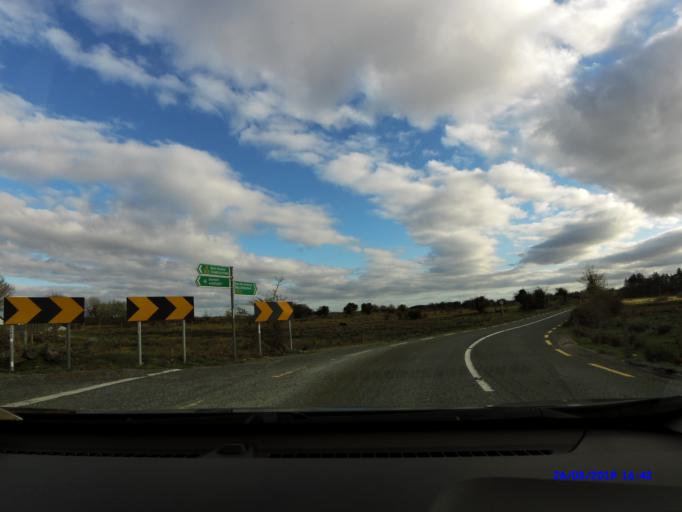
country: IE
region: Connaught
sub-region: Maigh Eo
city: Ballyhaunis
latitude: 53.8658
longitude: -8.7631
